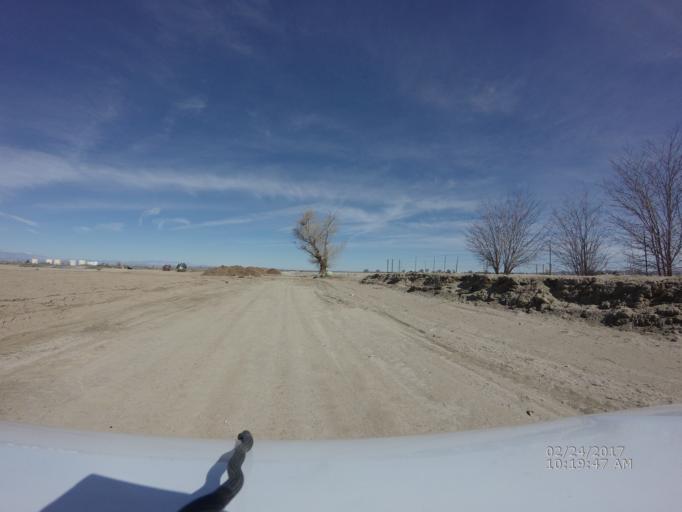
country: US
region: California
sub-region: Los Angeles County
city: Littlerock
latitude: 34.6676
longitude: -117.9874
